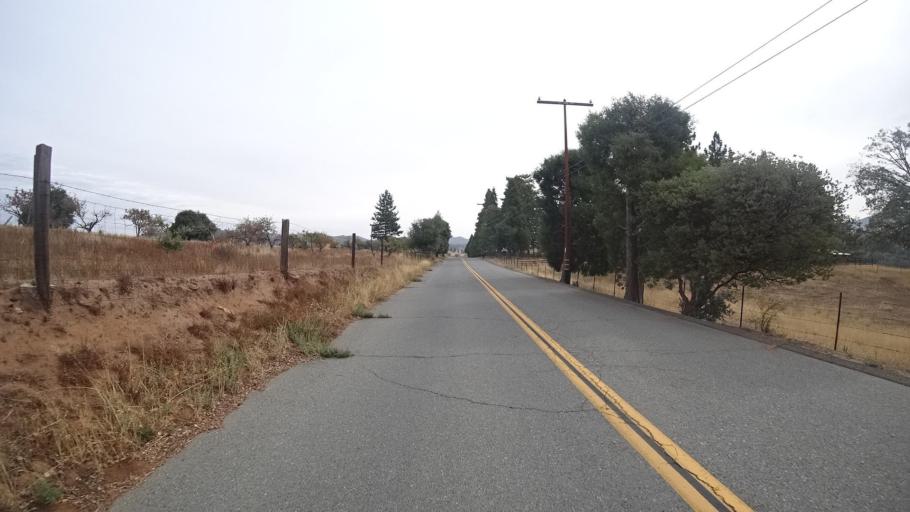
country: US
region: California
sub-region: San Diego County
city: Julian
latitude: 33.0481
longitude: -116.6178
